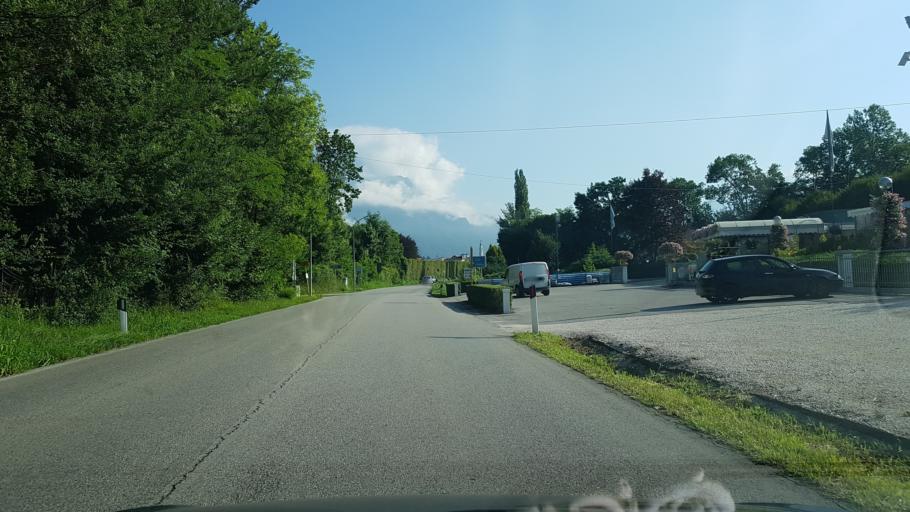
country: IT
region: Veneto
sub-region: Provincia di Belluno
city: Belluno
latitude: 46.1233
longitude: 12.2058
